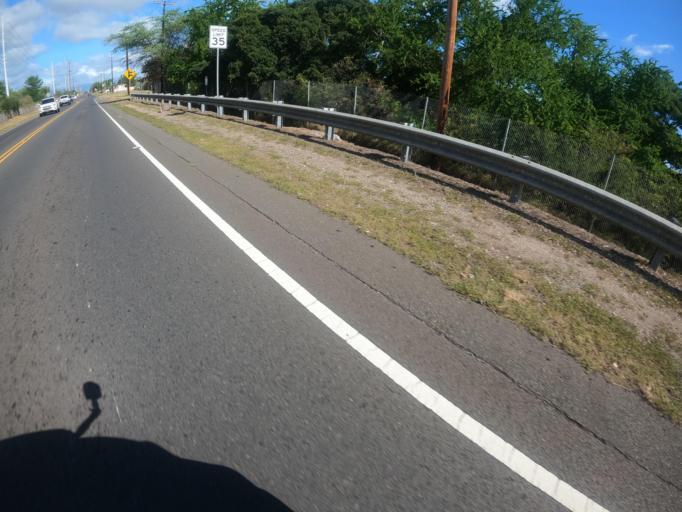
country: US
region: Hawaii
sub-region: Honolulu County
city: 'Ewa Villages
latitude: 21.3255
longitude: -158.0656
